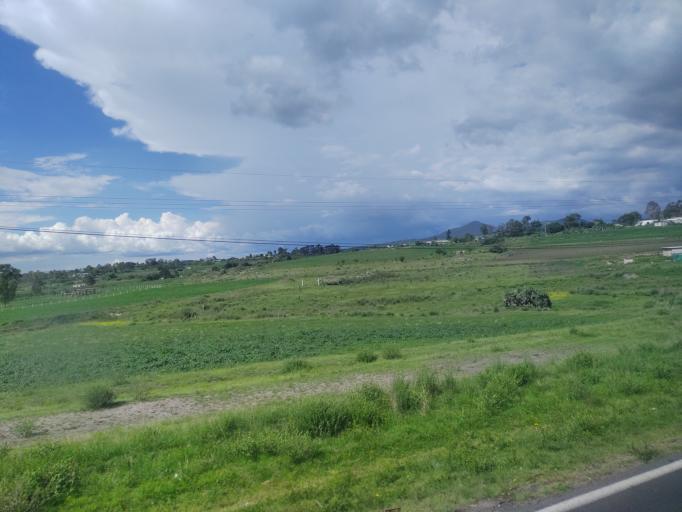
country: MX
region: Mexico
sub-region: Aculco
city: El Colorado
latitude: 20.0962
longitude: -99.7562
